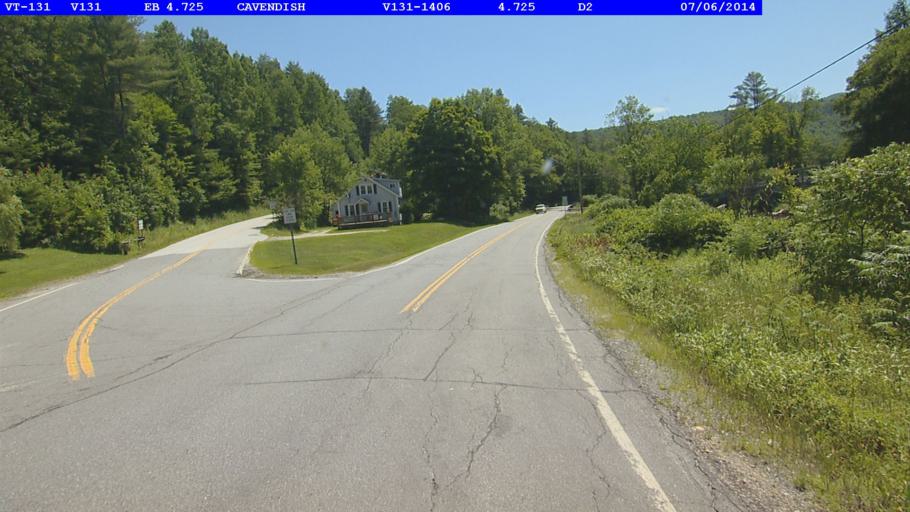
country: US
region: Vermont
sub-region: Windsor County
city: Springfield
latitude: 43.4051
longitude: -72.5763
